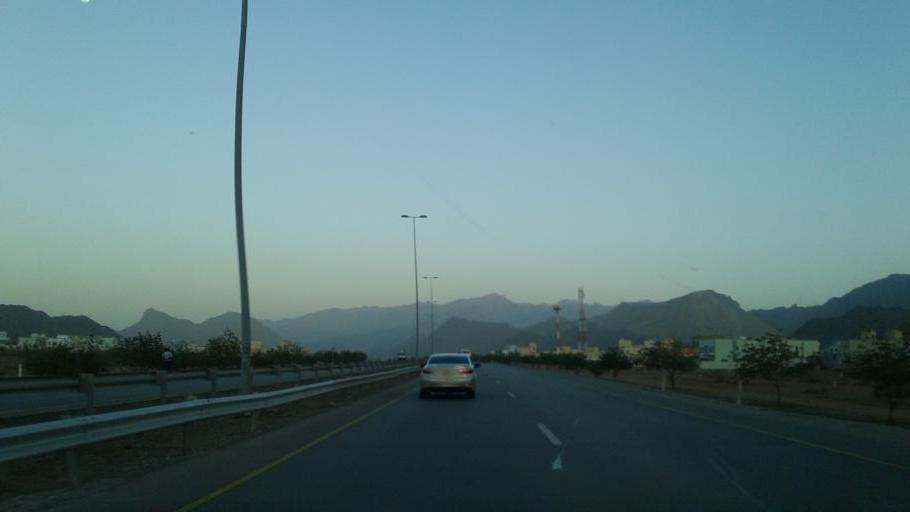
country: OM
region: Muhafazat ad Dakhiliyah
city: Bidbid
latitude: 23.4652
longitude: 58.1494
